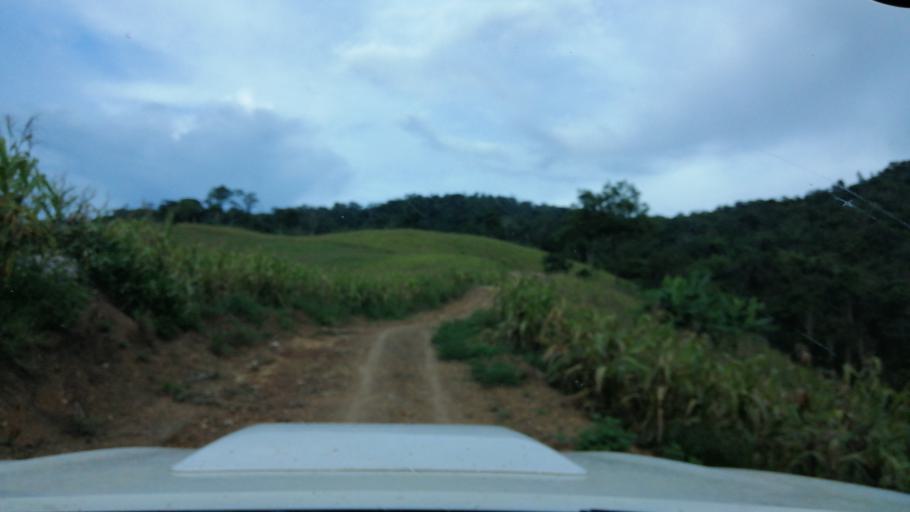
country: TH
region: Nan
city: Chaloem Phra Kiat
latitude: 19.7569
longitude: 101.1099
